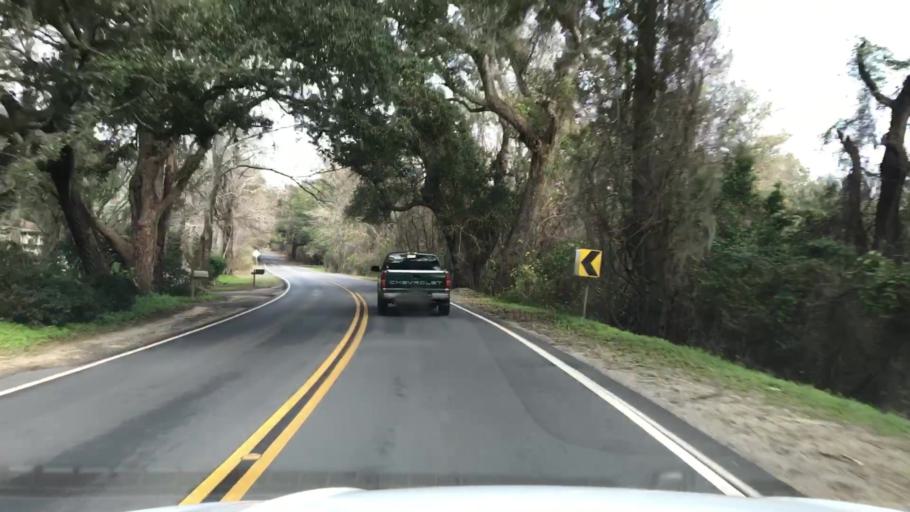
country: US
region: South Carolina
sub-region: Charleston County
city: Folly Beach
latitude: 32.6911
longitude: -80.0167
